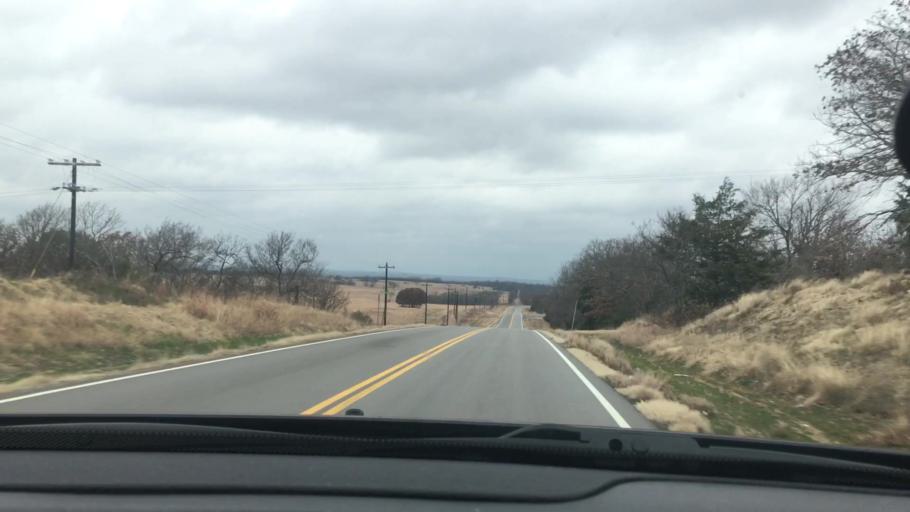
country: US
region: Oklahoma
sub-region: Atoka County
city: Atoka
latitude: 34.3749
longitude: -96.2494
